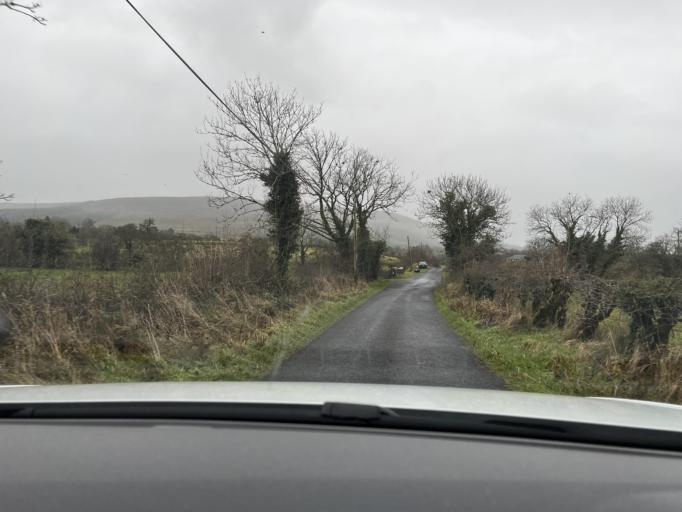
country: IE
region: Connaught
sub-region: County Leitrim
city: Manorhamilton
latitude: 54.2928
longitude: -8.0827
